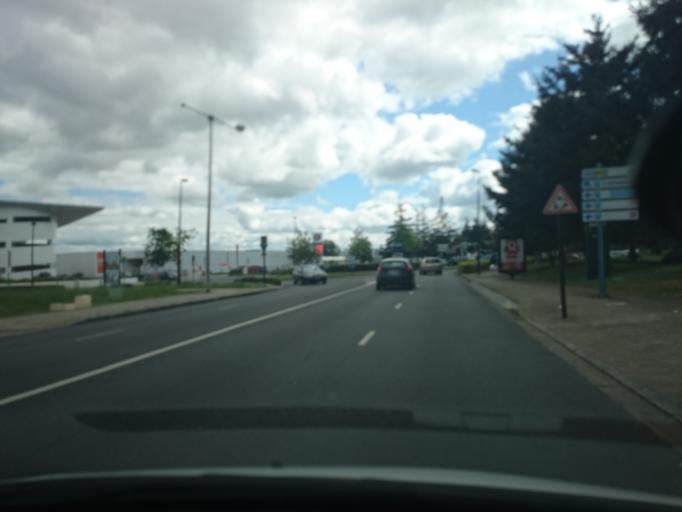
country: FR
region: Pays de la Loire
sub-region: Departement de la Loire-Atlantique
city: Saint-Herblain
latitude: 47.2270
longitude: -1.6348
